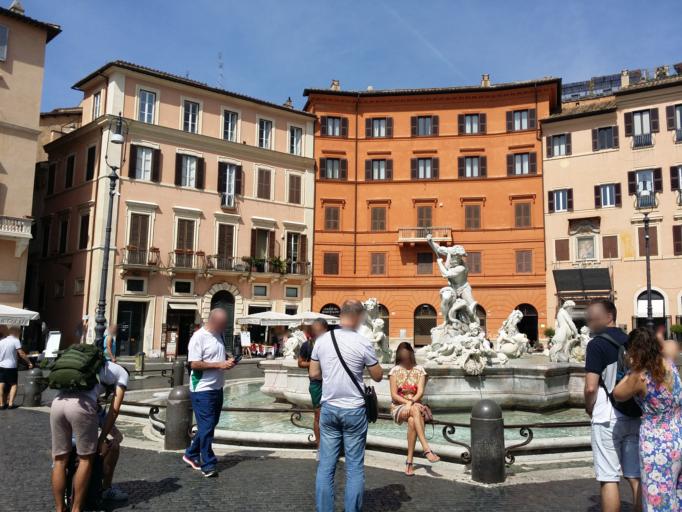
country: VA
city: Vatican City
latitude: 41.8997
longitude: 12.4730
